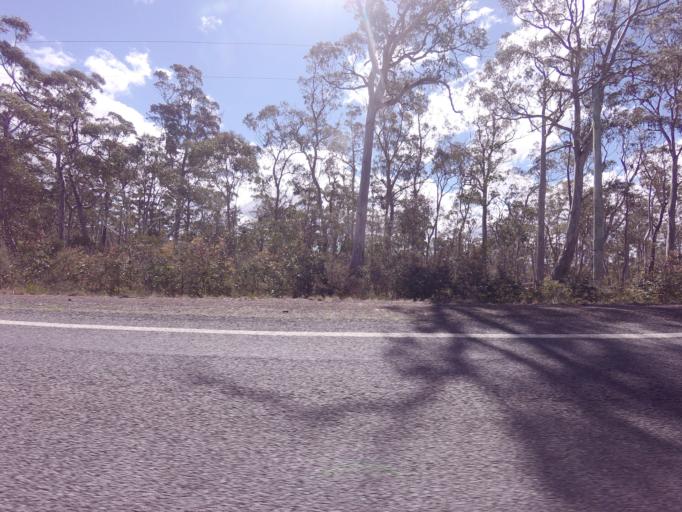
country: AU
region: Tasmania
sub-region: Northern Midlands
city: Evandale
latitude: -42.0263
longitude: 147.8363
